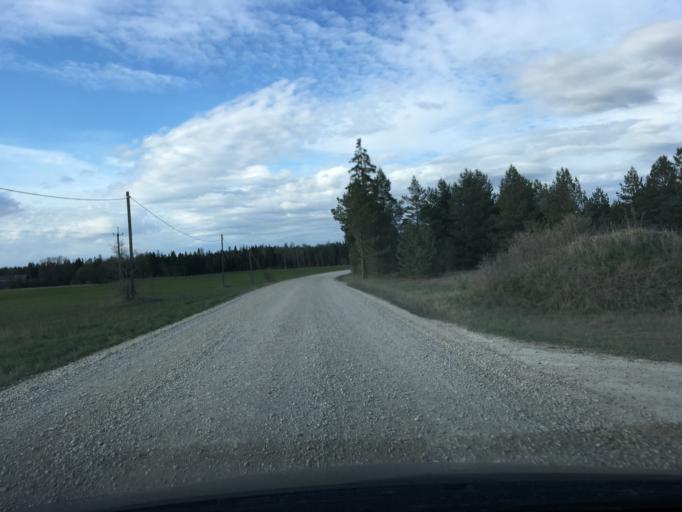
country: EE
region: Raplamaa
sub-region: Maerjamaa vald
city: Marjamaa
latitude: 58.9475
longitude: 24.3193
